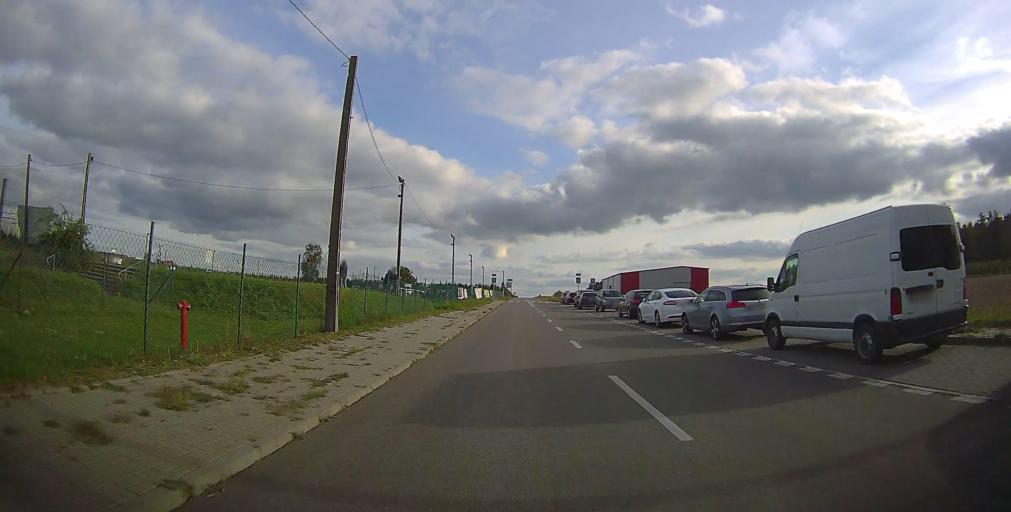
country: PL
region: Masovian Voivodeship
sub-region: Powiat grojecki
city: Jasieniec
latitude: 51.7557
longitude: 20.9625
